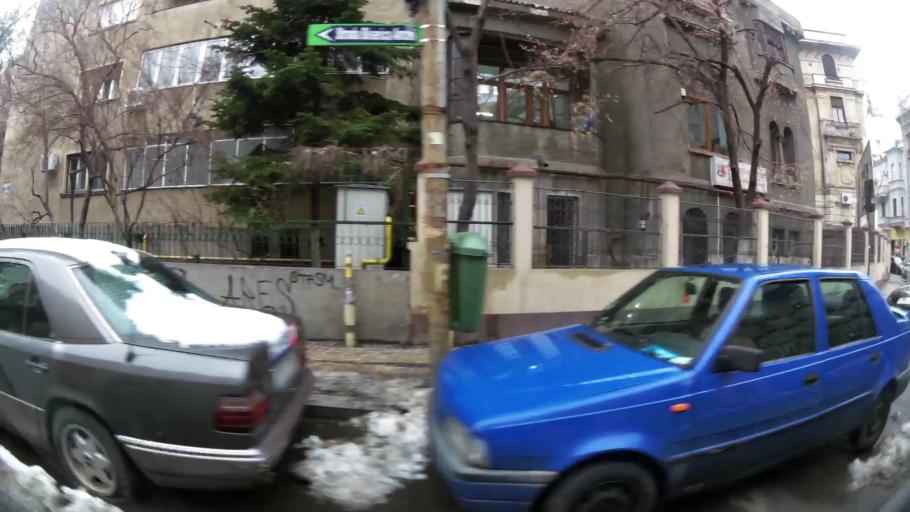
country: RO
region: Bucuresti
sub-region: Municipiul Bucuresti
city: Bucharest
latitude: 44.4455
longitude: 26.0961
